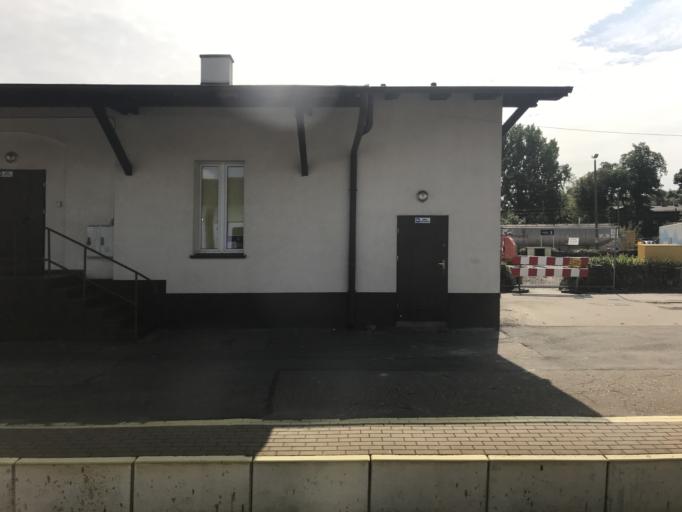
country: PL
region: Kujawsko-Pomorskie
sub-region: Powiat inowroclawski
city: Inowroclaw
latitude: 52.8060
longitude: 18.2442
